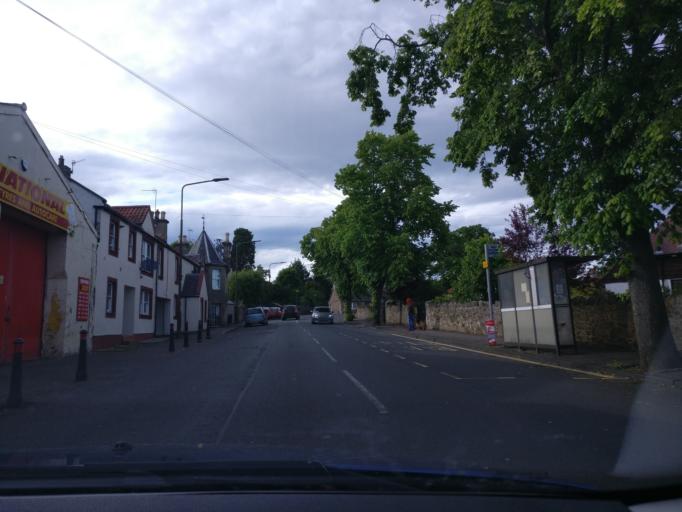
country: GB
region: Scotland
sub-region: East Lothian
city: Haddington
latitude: 55.9595
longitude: -2.7765
